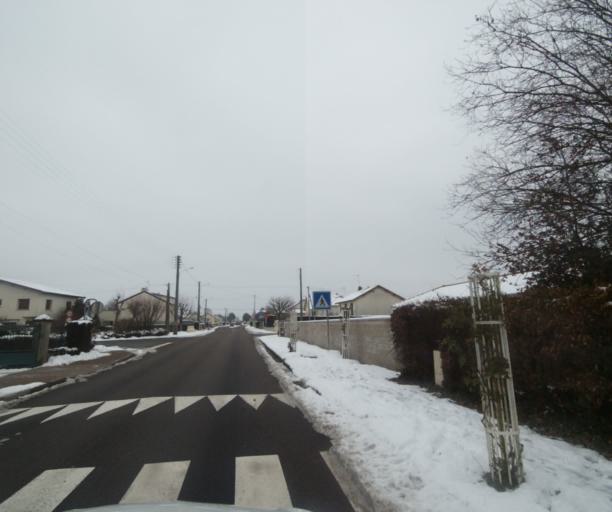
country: FR
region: Champagne-Ardenne
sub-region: Departement de la Haute-Marne
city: Villiers-en-Lieu
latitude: 48.5939
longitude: 4.8699
